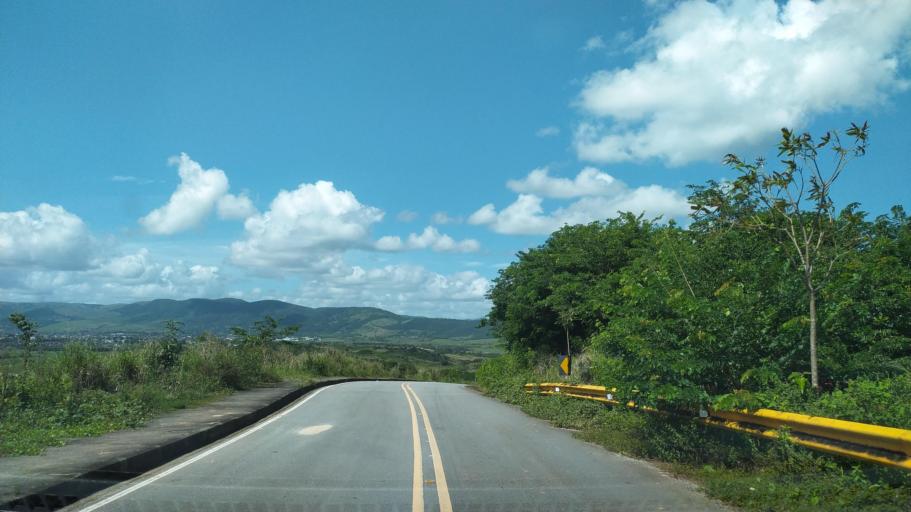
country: BR
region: Alagoas
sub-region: Uniao Dos Palmares
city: Uniao dos Palmares
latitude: -9.1676
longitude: -36.0643
